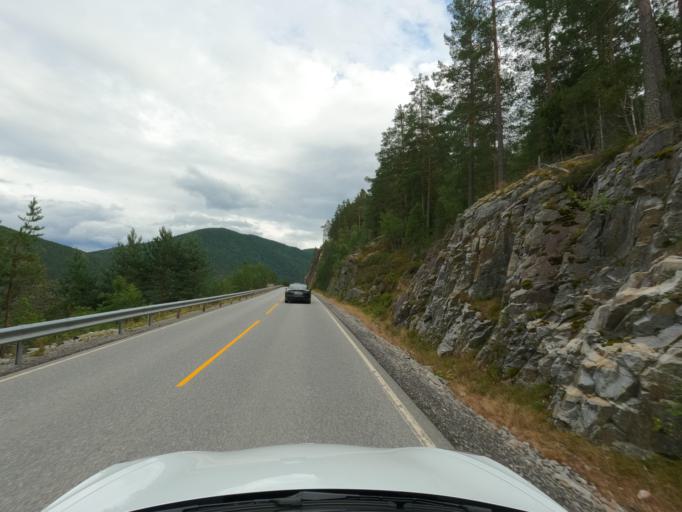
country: NO
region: Telemark
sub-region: Hjartdal
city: Sauland
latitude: 59.7716
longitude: 9.0136
